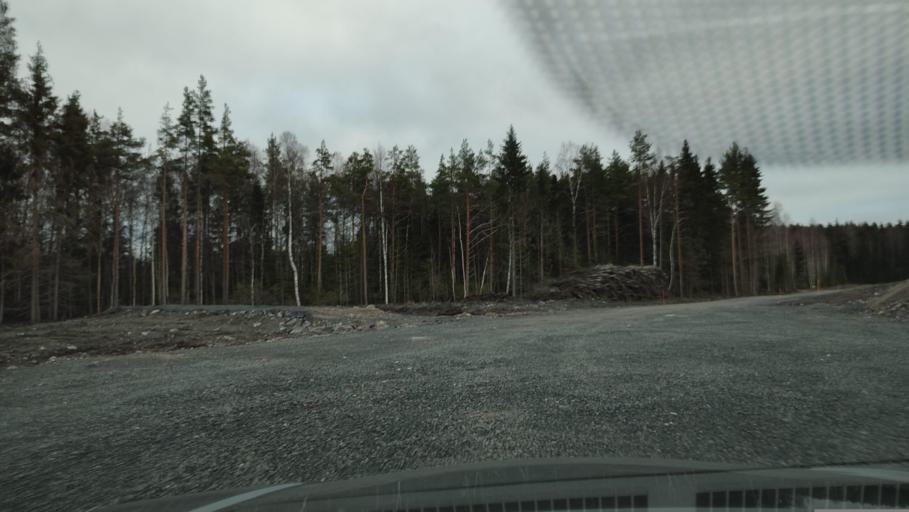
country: FI
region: Southern Ostrobothnia
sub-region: Suupohja
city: Karijoki
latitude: 62.2194
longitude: 21.5956
